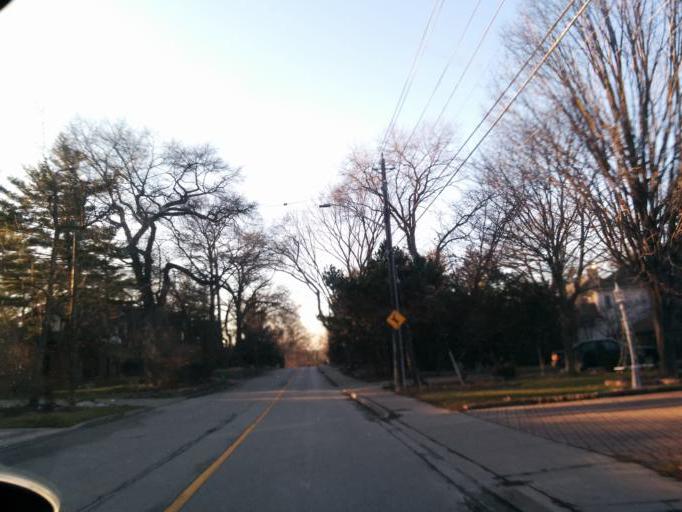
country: CA
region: Ontario
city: Mississauga
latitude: 43.5592
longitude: -79.6125
